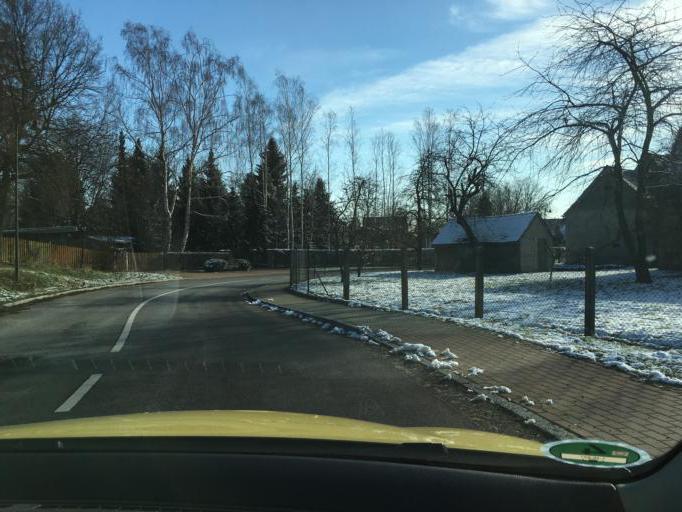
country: DE
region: Saxony
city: Belgershain
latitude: 51.2145
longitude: 12.5586
